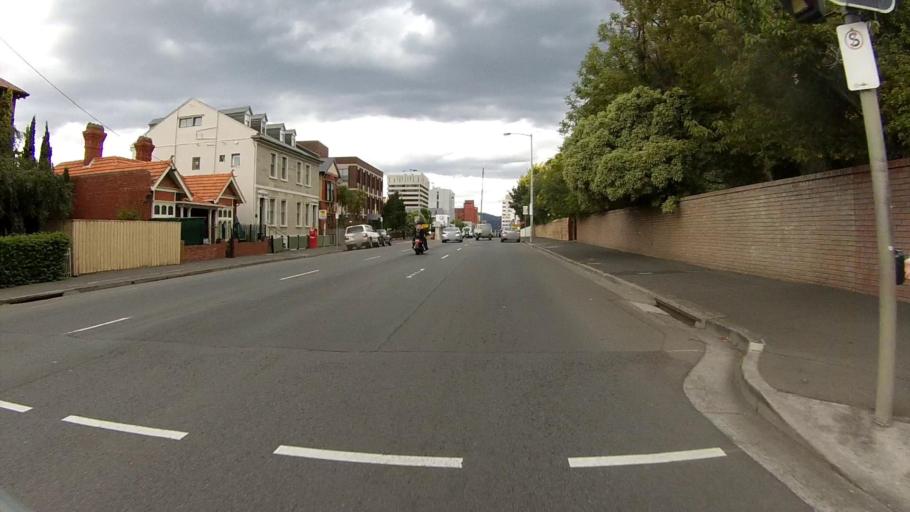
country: AU
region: Tasmania
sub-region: Hobart
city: Sandy Bay
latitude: -42.8885
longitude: 147.3228
